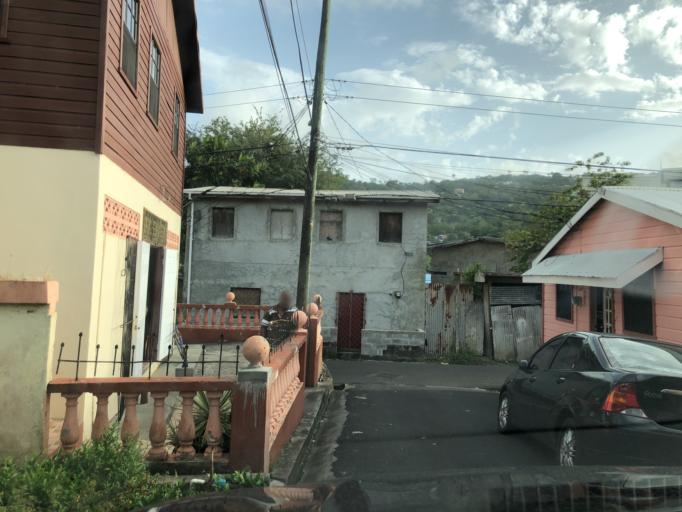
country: LC
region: Castries Quarter
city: Bisee
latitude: 14.0064
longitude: -60.9845
